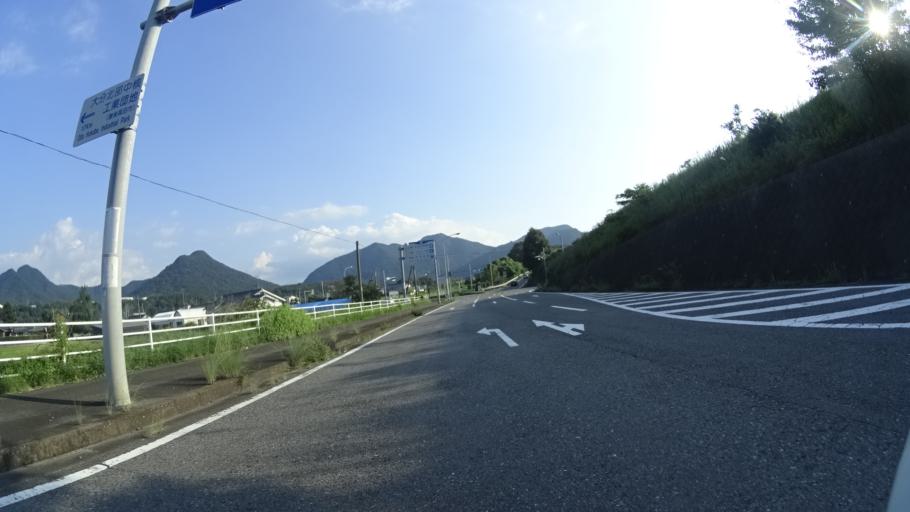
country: JP
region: Oita
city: Bungo-Takada-shi
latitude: 33.5111
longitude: 131.3262
